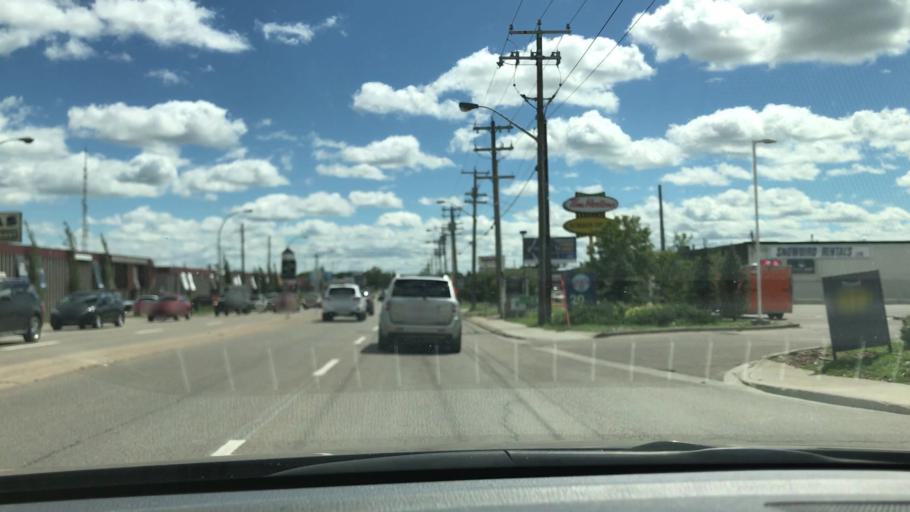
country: CA
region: Alberta
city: Edmonton
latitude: 53.4879
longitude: -113.4862
